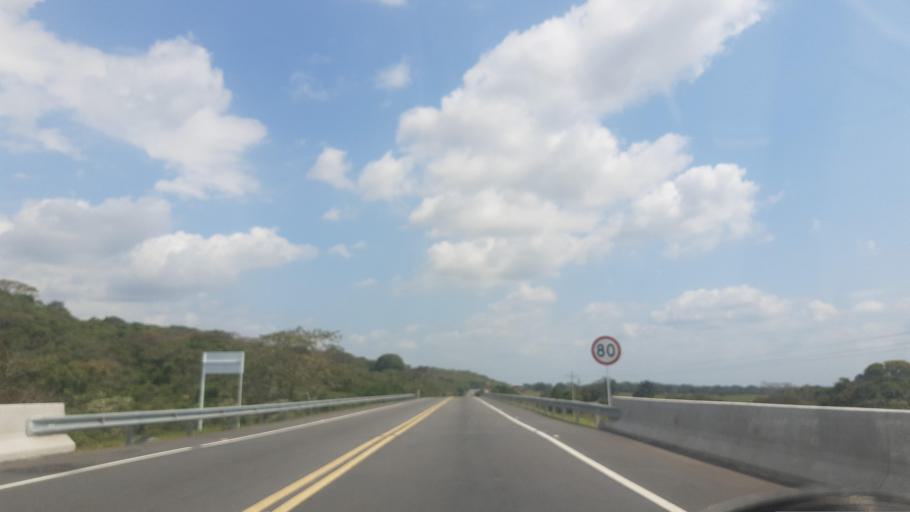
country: CO
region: Casanare
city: Tauramena
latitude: 4.8872
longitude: -72.6901
